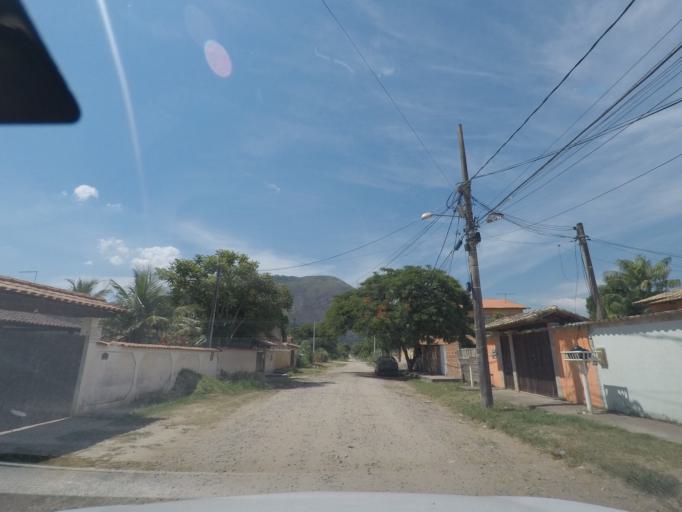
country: BR
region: Rio de Janeiro
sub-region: Marica
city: Marica
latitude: -22.9528
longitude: -42.9604
